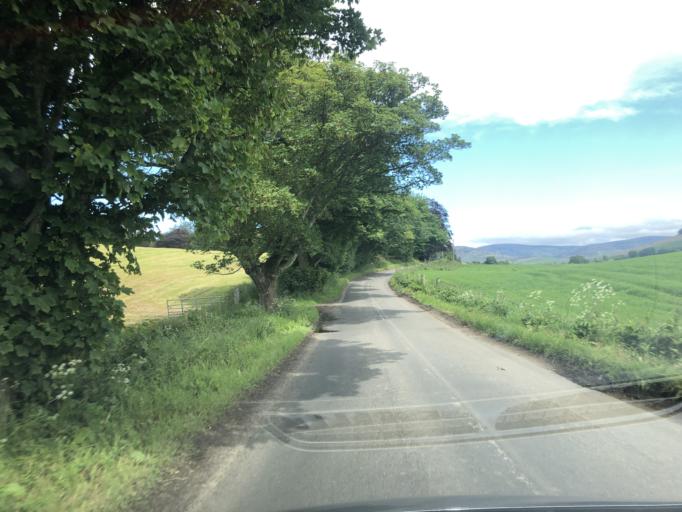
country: GB
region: Scotland
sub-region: Angus
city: Kirriemuir
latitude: 56.7327
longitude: -3.0044
